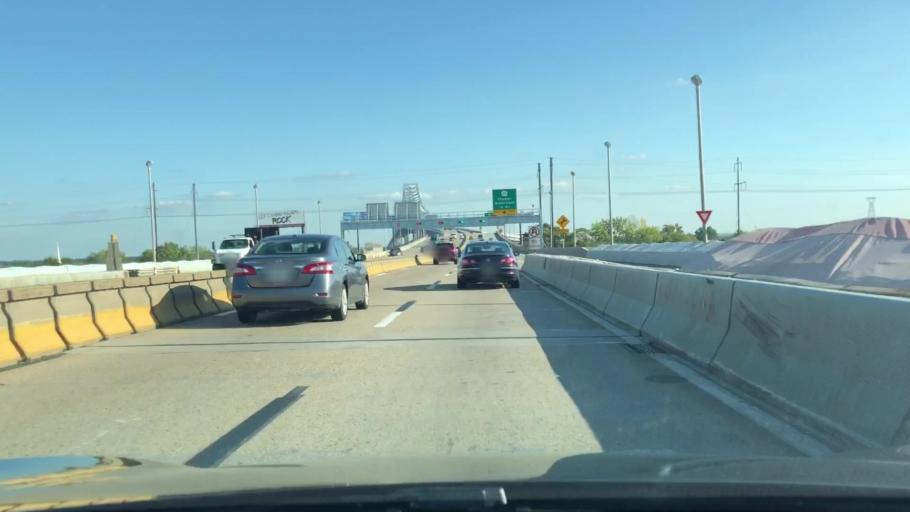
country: US
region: Pennsylvania
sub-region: Delaware County
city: Upland
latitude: 39.8403
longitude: -75.3832
